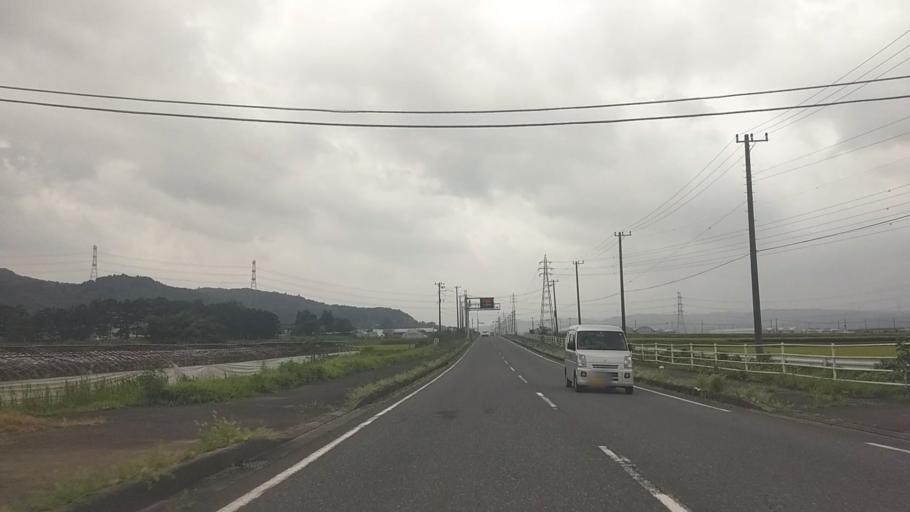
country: JP
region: Chiba
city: Kisarazu
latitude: 35.3532
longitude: 140.0548
